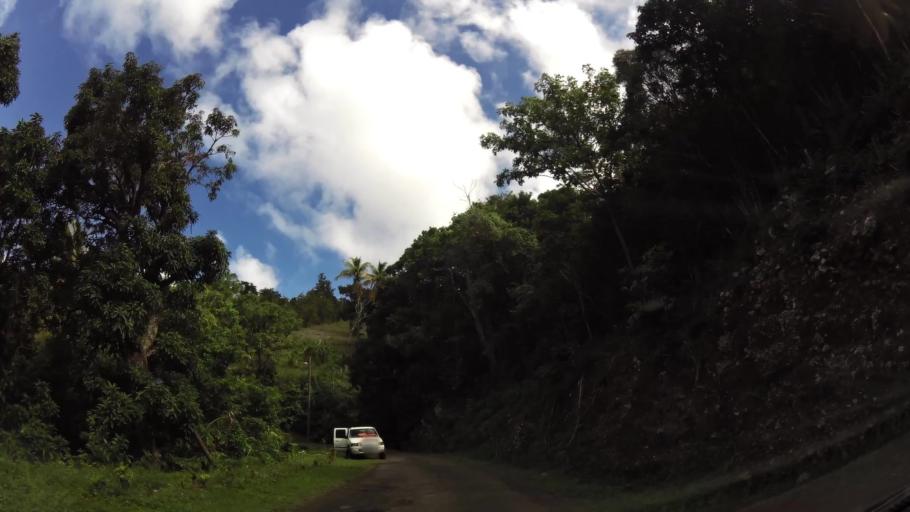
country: DM
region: Saint John
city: Portsmouth
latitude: 15.6322
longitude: -61.4599
